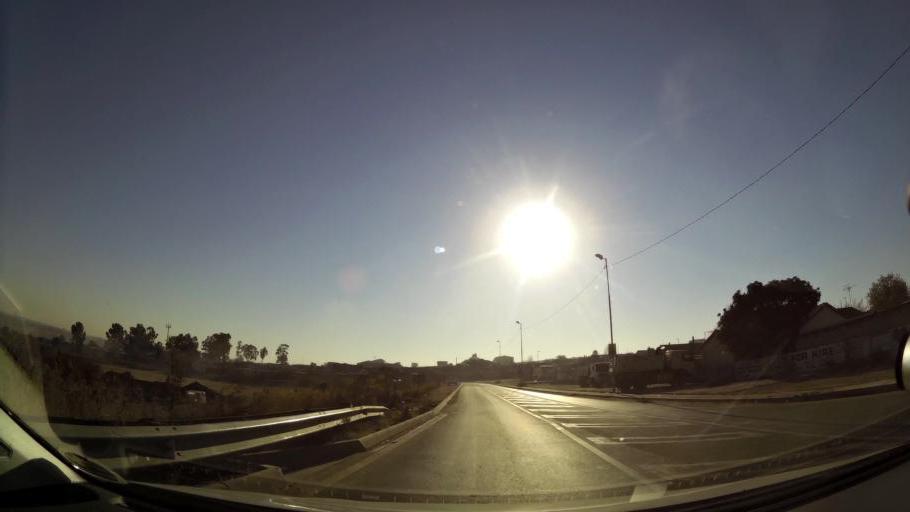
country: ZA
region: Gauteng
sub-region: City of Johannesburg Metropolitan Municipality
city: Modderfontein
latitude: -26.0497
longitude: 28.1586
